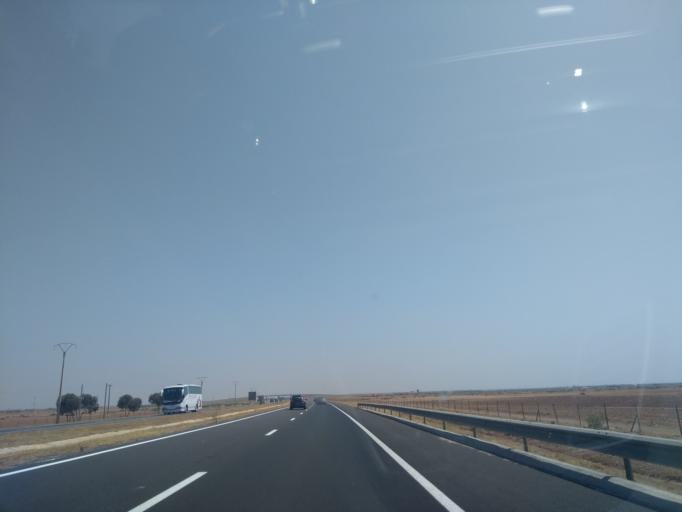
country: MA
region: Marrakech-Tensift-Al Haouz
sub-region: Kelaa-Des-Sraghna
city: Sidi Bou Othmane
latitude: 31.9290
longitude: -8.0197
